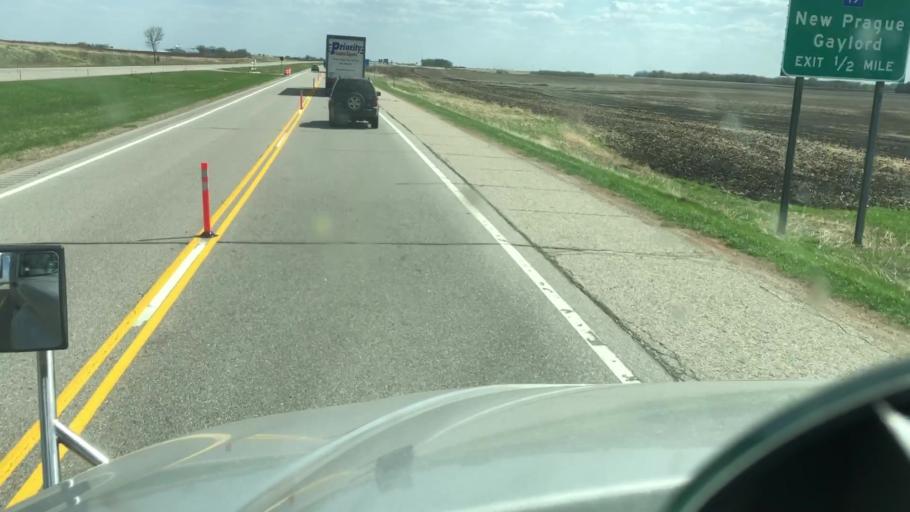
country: US
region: Minnesota
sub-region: Scott County
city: Belle Plaine
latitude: 44.5559
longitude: -93.8509
